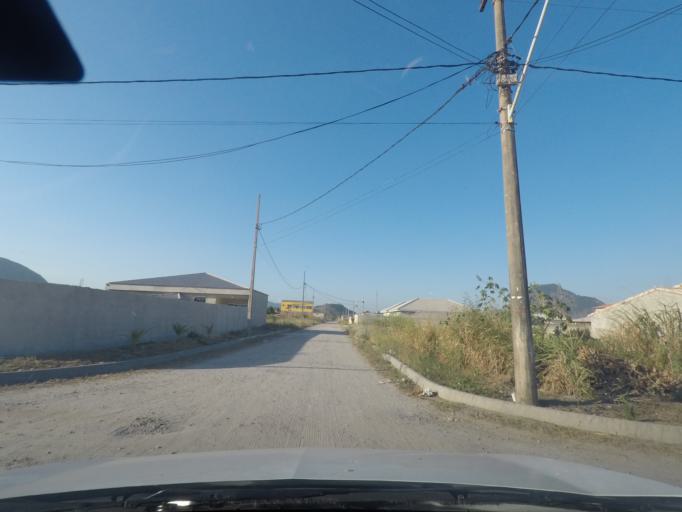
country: BR
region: Rio de Janeiro
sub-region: Marica
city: Marica
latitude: -22.9620
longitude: -42.9352
